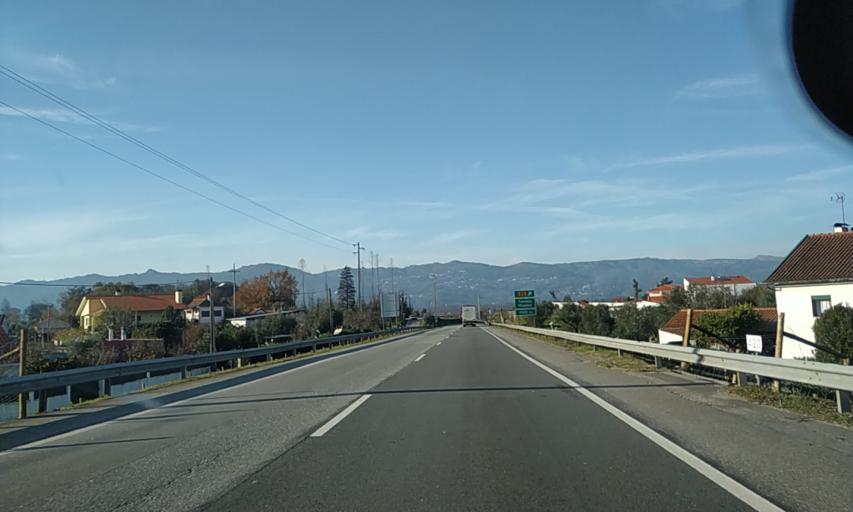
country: PT
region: Viseu
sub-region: Concelho de Tondela
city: Tondela
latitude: 40.5133
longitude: -8.0900
